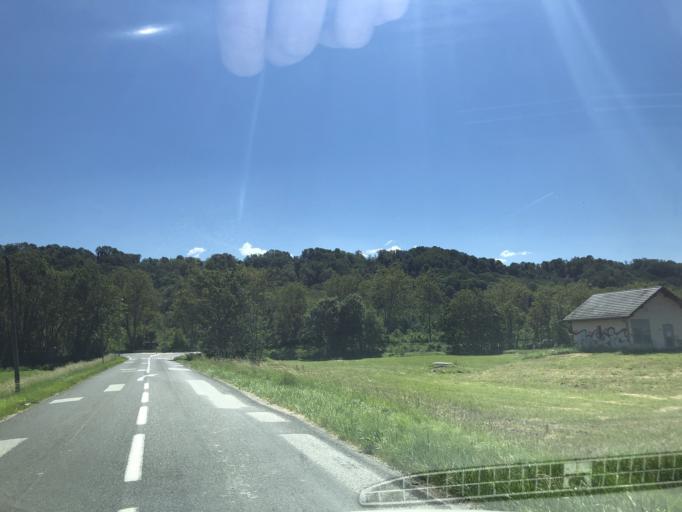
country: FR
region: Rhone-Alpes
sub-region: Departement de la Savoie
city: Coise-Saint-Jean-Pied-Gauthier
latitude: 45.5423
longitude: 6.1349
